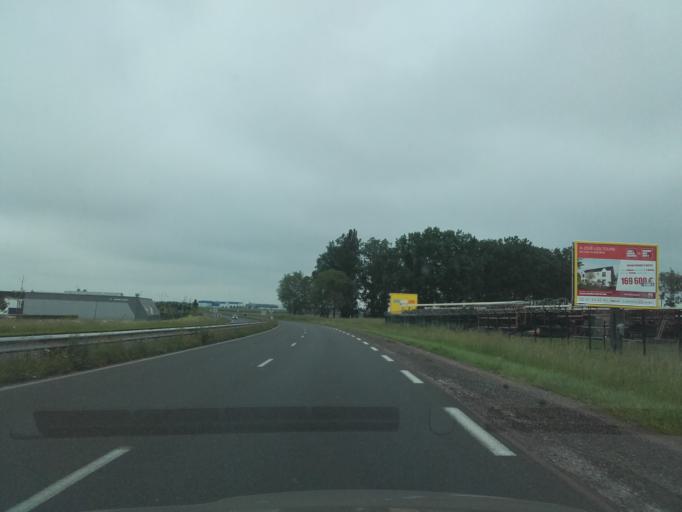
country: FR
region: Centre
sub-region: Departement d'Indre-et-Loire
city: Parcay-Meslay
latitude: 47.4395
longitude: 0.7154
